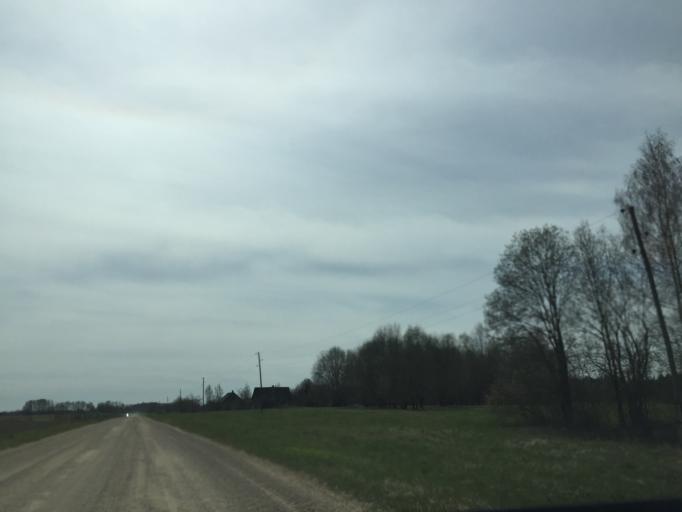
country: LV
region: Ludzas Rajons
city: Ludza
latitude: 56.5749
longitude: 27.5499
